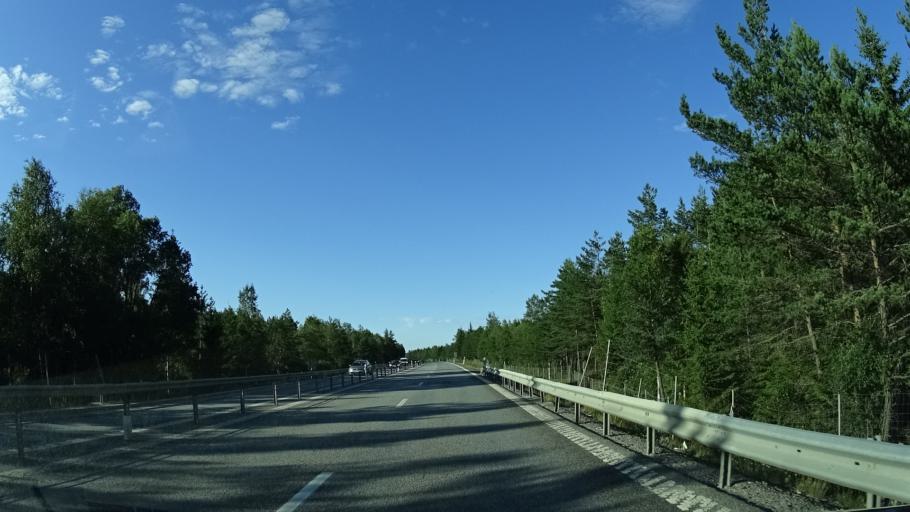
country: SE
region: Stockholm
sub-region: Osterakers Kommun
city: Akersberga
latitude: 59.5968
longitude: 18.2713
